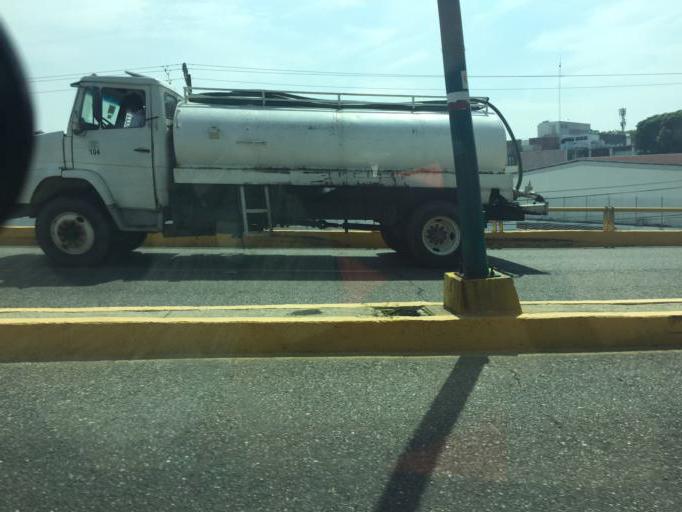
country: MX
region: Guerrero
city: Acapulco de Juarez
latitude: 16.8572
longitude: -99.9010
